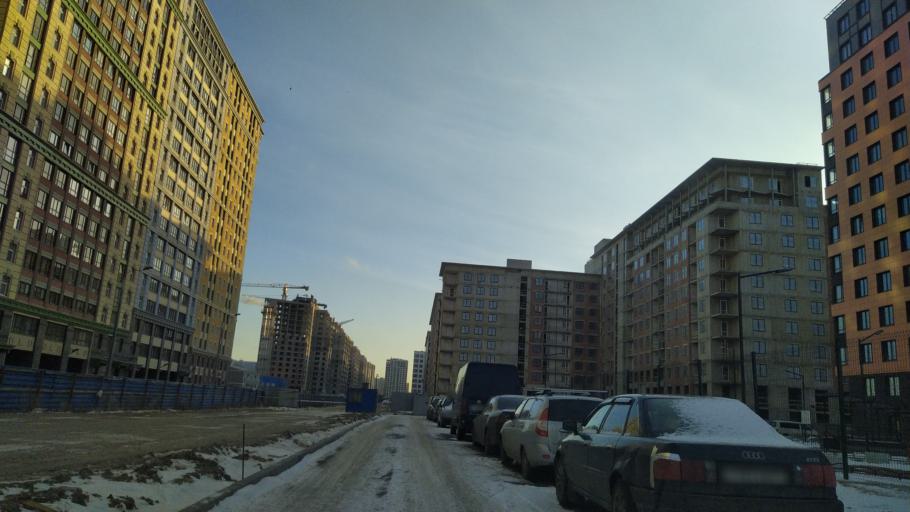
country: RU
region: St.-Petersburg
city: Admiralteisky
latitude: 59.9051
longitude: 30.3116
